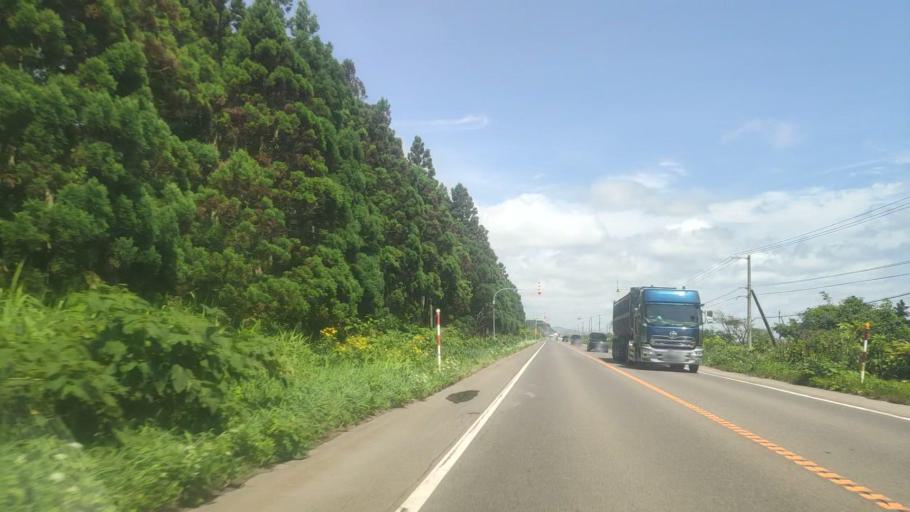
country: JP
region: Hokkaido
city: Niseko Town
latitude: 42.3422
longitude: 140.2812
